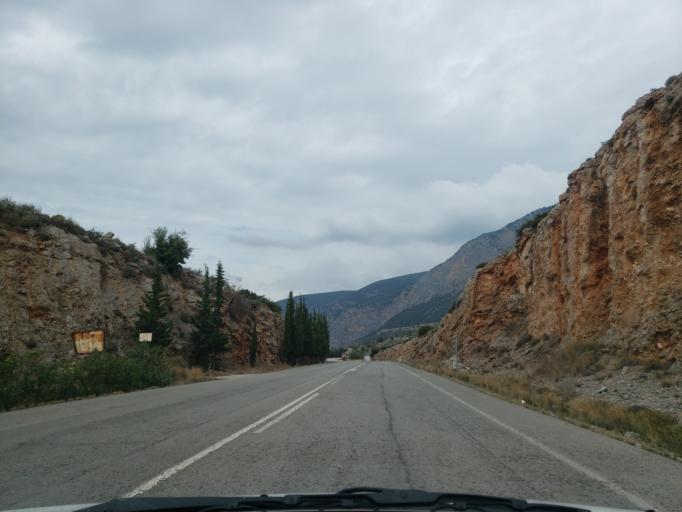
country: GR
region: Central Greece
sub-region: Nomos Fokidos
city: Delphi
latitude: 38.4776
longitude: 22.4630
